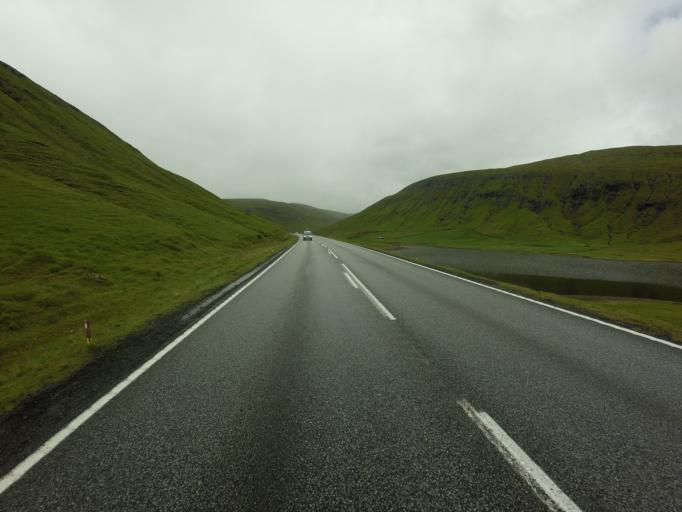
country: FO
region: Streymoy
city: Kollafjordhur
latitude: 62.1268
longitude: -7.0026
